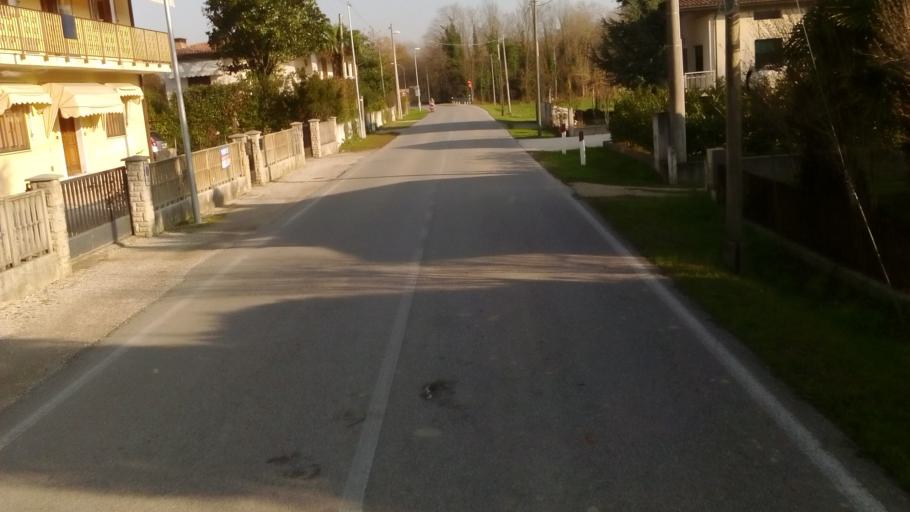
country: IT
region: Friuli Venezia Giulia
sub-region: Provincia di Udine
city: Precenicco
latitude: 45.8133
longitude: 13.0792
